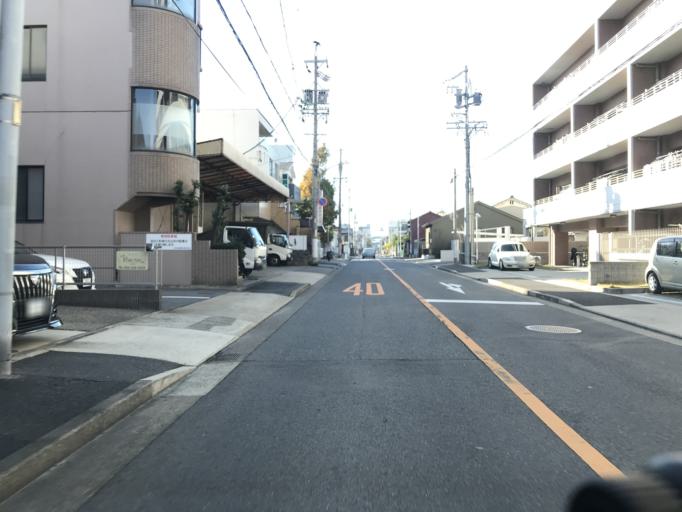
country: JP
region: Aichi
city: Nagoya-shi
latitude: 35.1895
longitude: 136.9224
